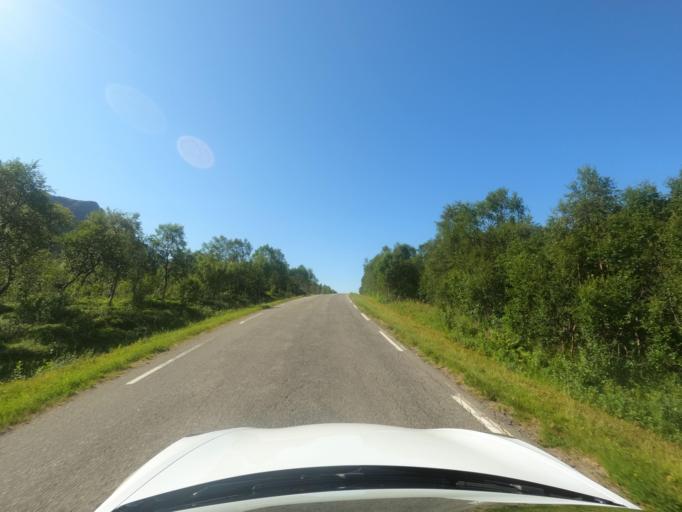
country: NO
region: Nordland
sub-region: Hadsel
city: Stokmarknes
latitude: 68.3509
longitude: 15.0656
